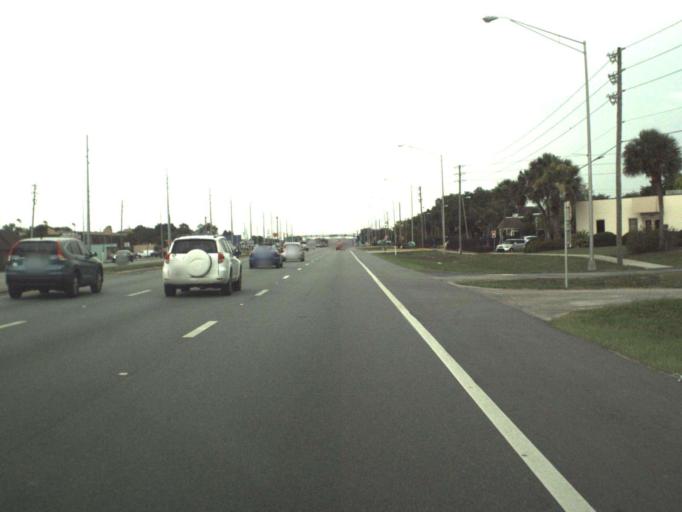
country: US
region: Florida
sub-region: Seminole County
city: Fern Park
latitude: 28.6550
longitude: -81.3330
